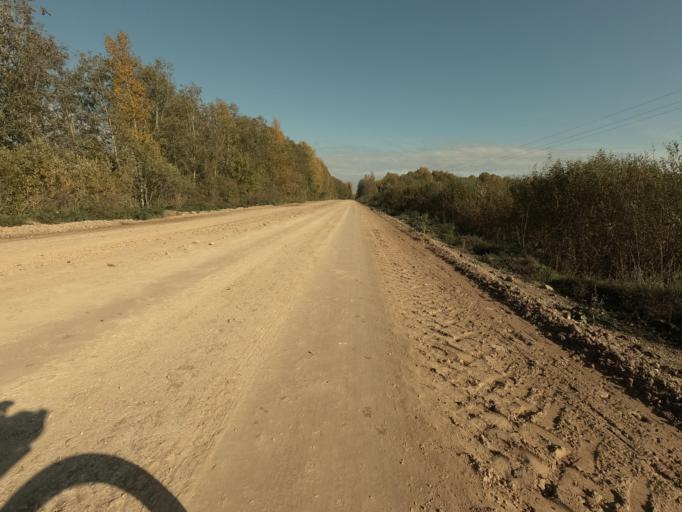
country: RU
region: Novgorod
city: Batetskiy
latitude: 58.8245
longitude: 30.7075
